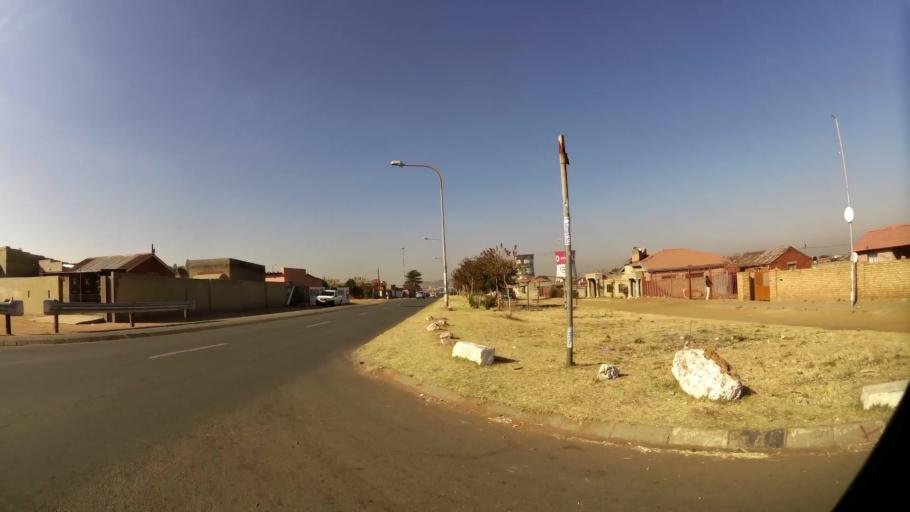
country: ZA
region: Gauteng
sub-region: City of Johannesburg Metropolitan Municipality
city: Soweto
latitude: -26.2462
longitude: 27.9250
